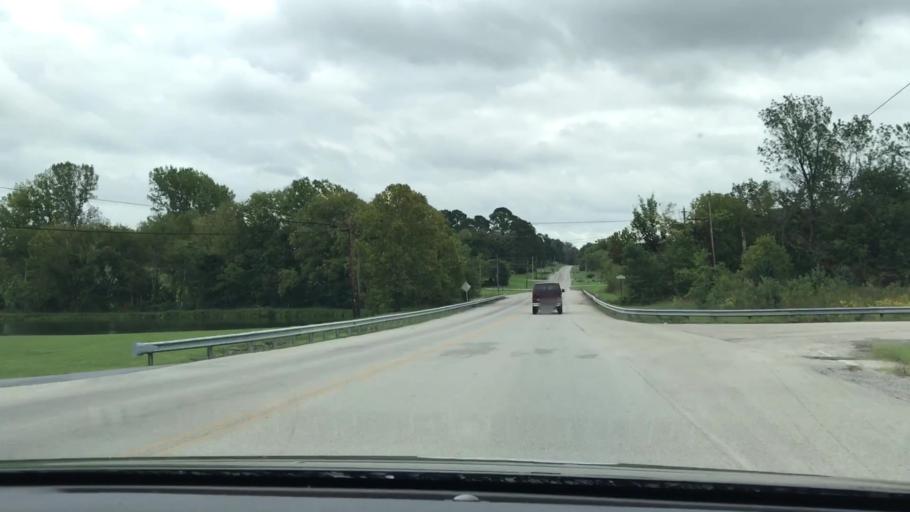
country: US
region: Kentucky
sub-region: Barren County
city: Glasgow
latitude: 36.9660
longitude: -85.8781
